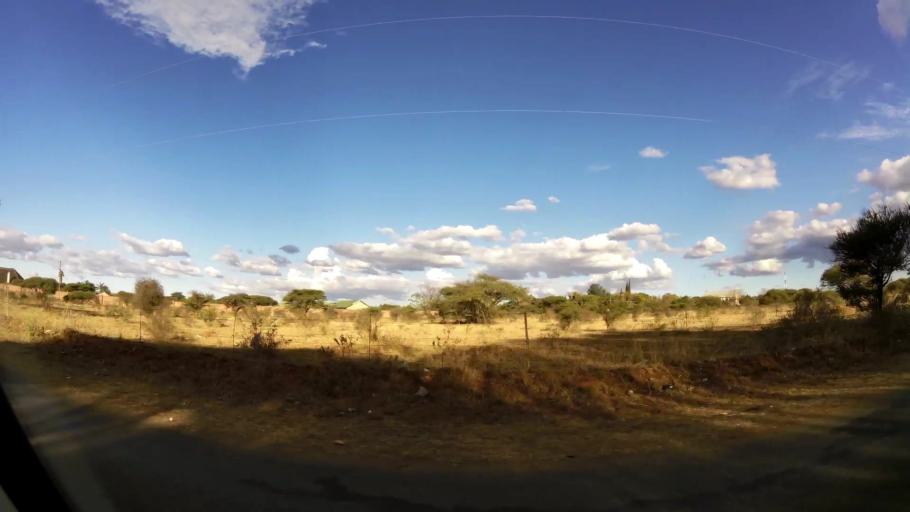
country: ZA
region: Limpopo
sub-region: Capricorn District Municipality
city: Polokwane
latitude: -23.9311
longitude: 29.4395
